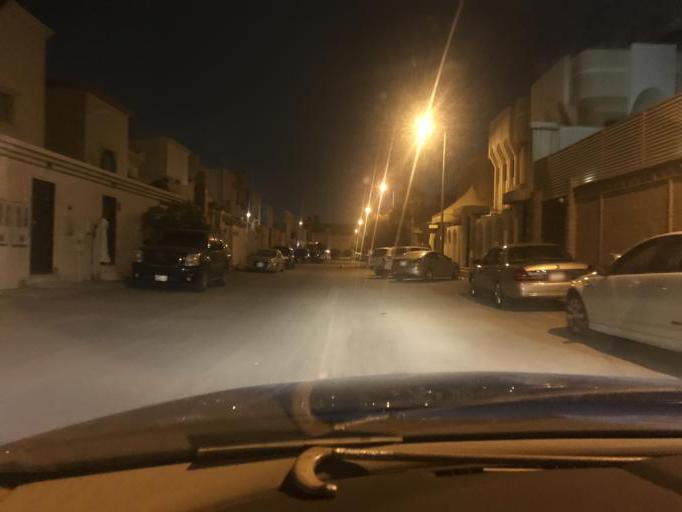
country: SA
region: Ar Riyad
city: Riyadh
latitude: 24.7512
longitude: 46.7761
